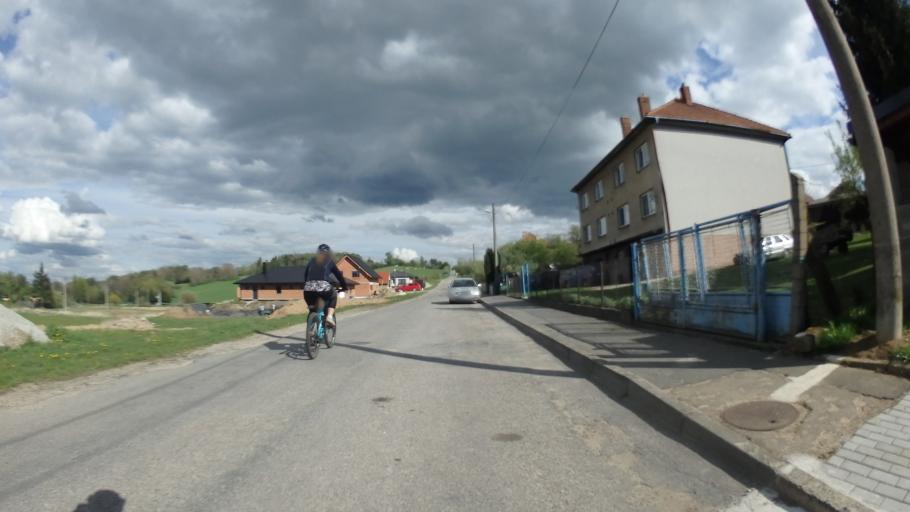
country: CZ
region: Vysocina
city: Merin
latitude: 49.3466
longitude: 15.8792
